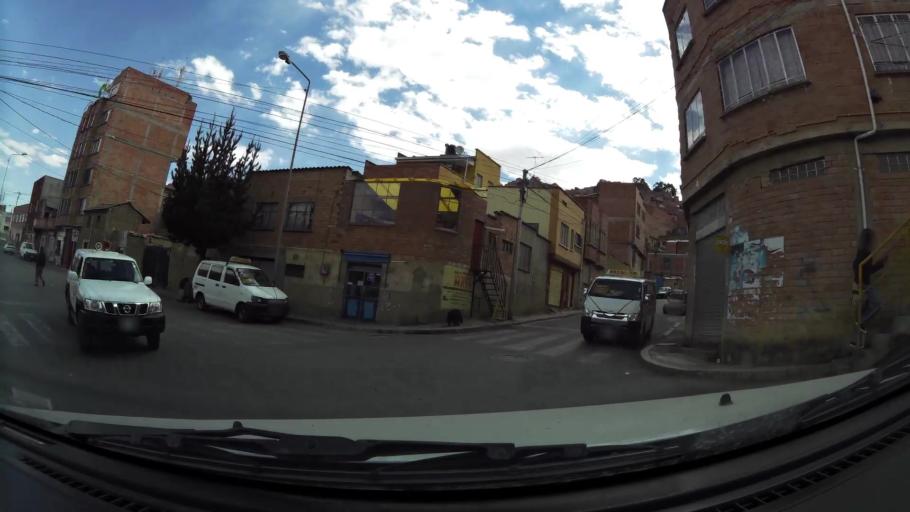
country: BO
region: La Paz
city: La Paz
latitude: -16.4762
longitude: -68.1230
